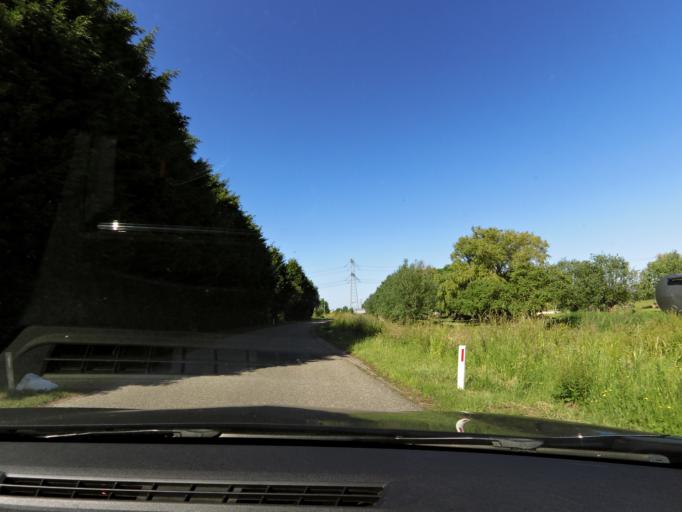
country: NL
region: South Holland
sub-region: Gemeente Brielle
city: Brielle
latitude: 51.8802
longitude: 4.1617
